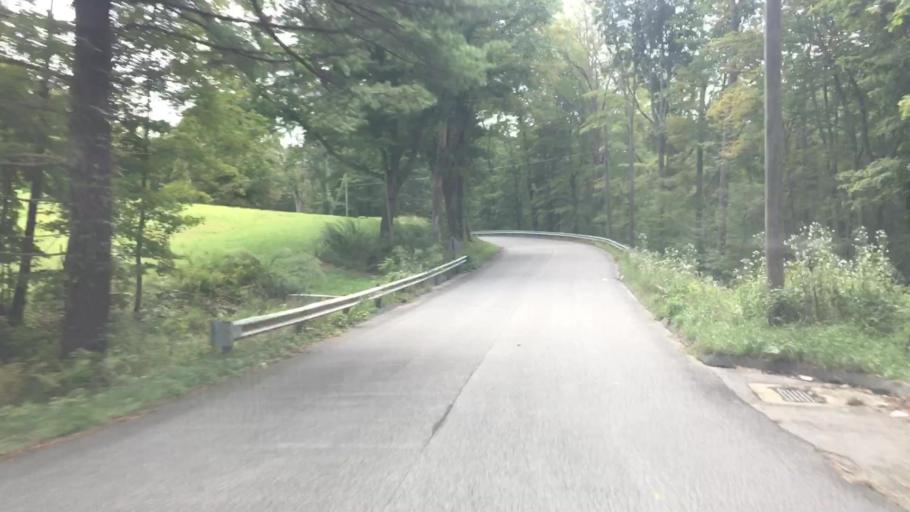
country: US
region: Connecticut
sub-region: Tolland County
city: Stafford Springs
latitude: 41.9183
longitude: -72.2249
